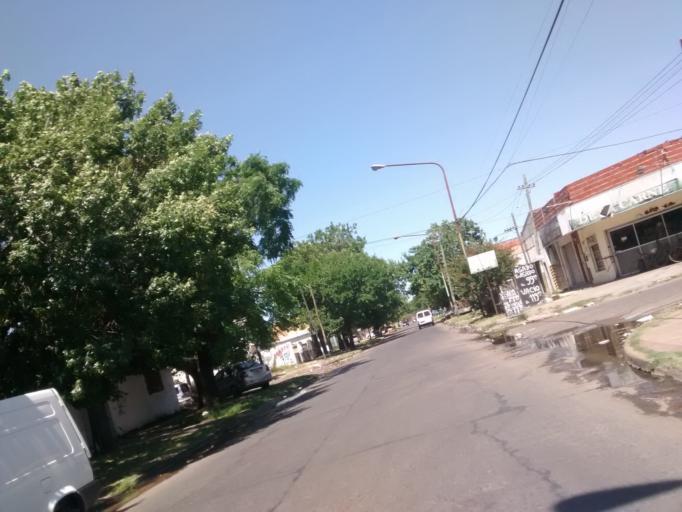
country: AR
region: Buenos Aires
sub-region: Partido de La Plata
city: La Plata
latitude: -34.9324
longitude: -57.9144
